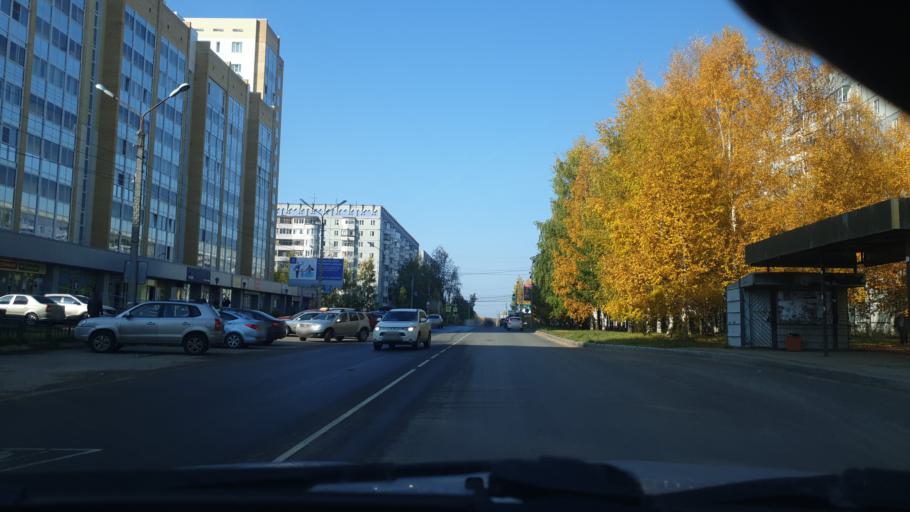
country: RU
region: Komi Republic
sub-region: Syktyvdinskiy Rayon
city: Syktyvkar
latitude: 61.6934
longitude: 50.8159
